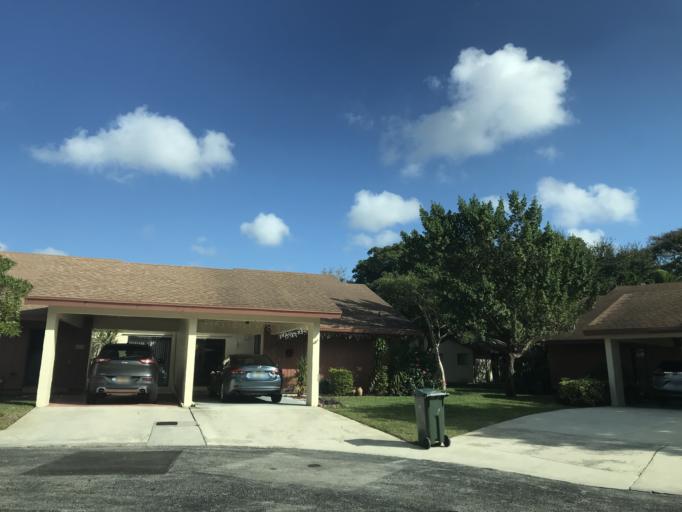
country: US
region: Florida
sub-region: Broward County
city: Coconut Creek
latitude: 26.2490
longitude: -80.1889
